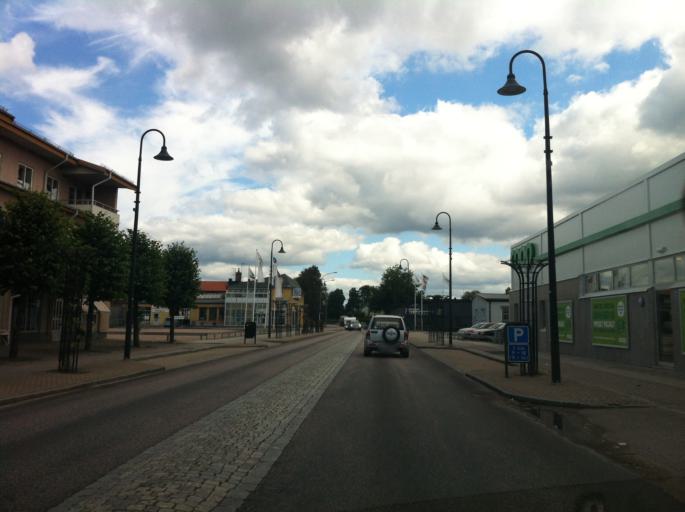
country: SE
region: Joenkoeping
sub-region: Gislaveds Kommun
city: Smalandsstenar
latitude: 57.1644
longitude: 13.4135
